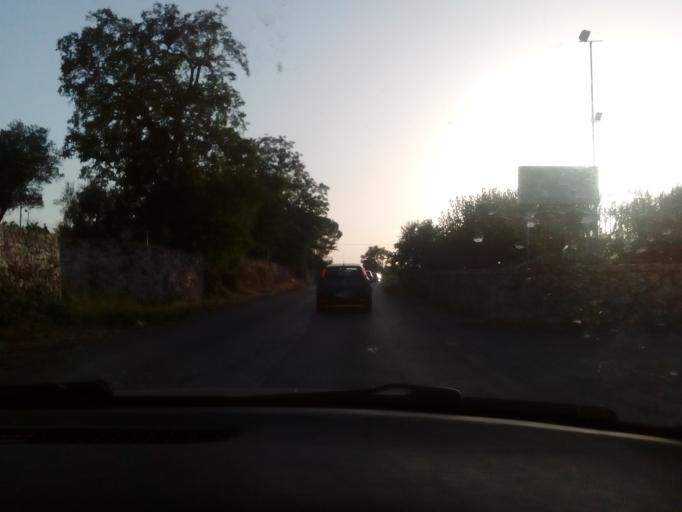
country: IT
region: Apulia
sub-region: Provincia di Bari
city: Altamura
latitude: 40.8421
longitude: 16.5718
